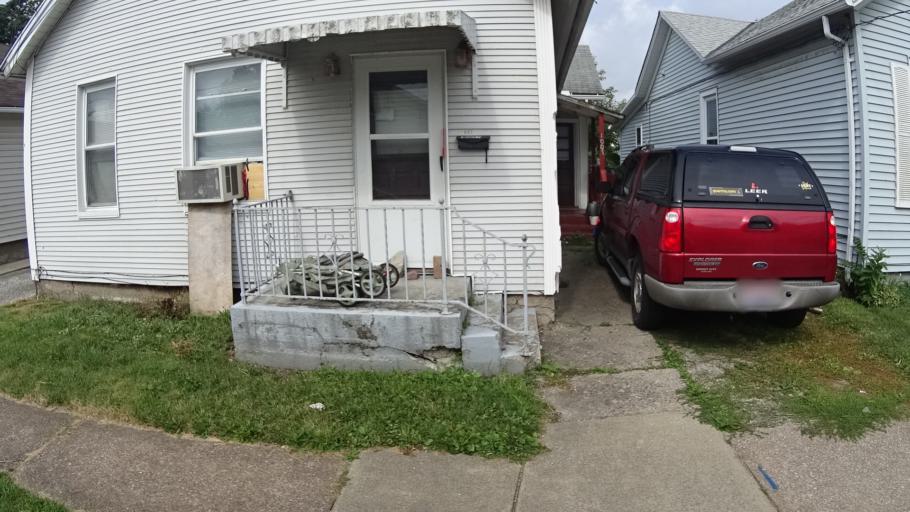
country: US
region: Ohio
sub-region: Erie County
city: Sandusky
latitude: 41.4460
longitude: -82.7168
